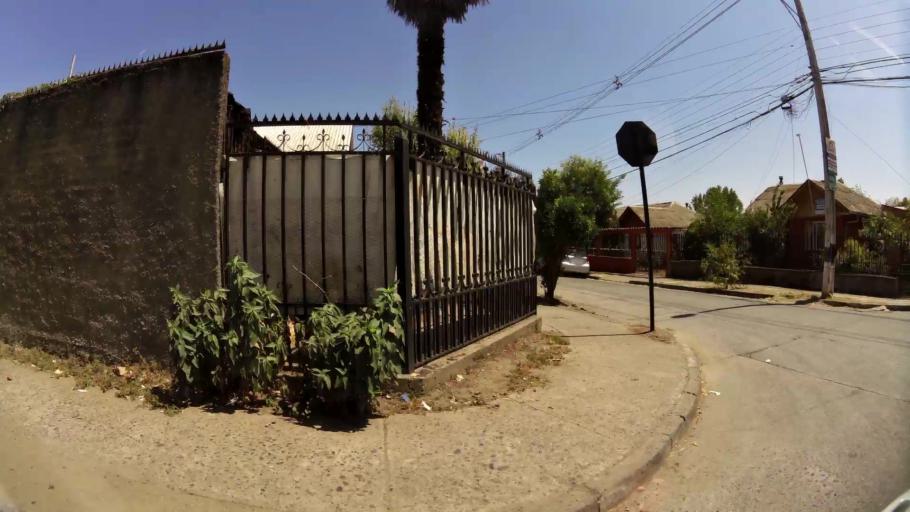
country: CL
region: Maule
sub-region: Provincia de Talca
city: Talca
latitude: -35.4288
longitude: -71.6343
